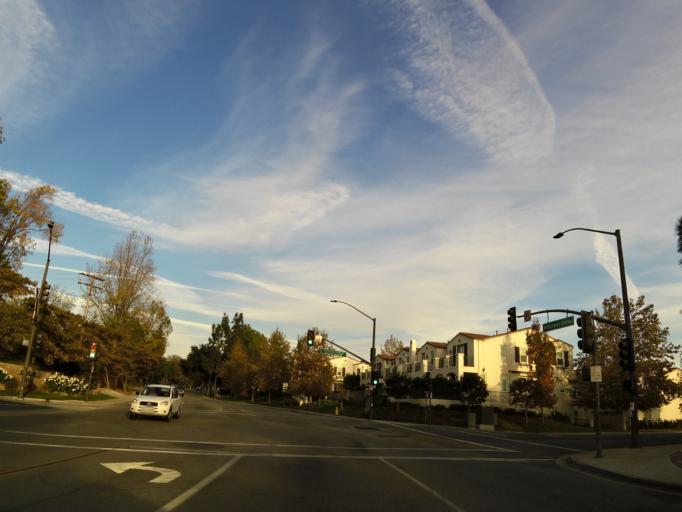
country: US
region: California
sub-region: Ventura County
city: Thousand Oaks
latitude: 34.1810
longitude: -118.8589
